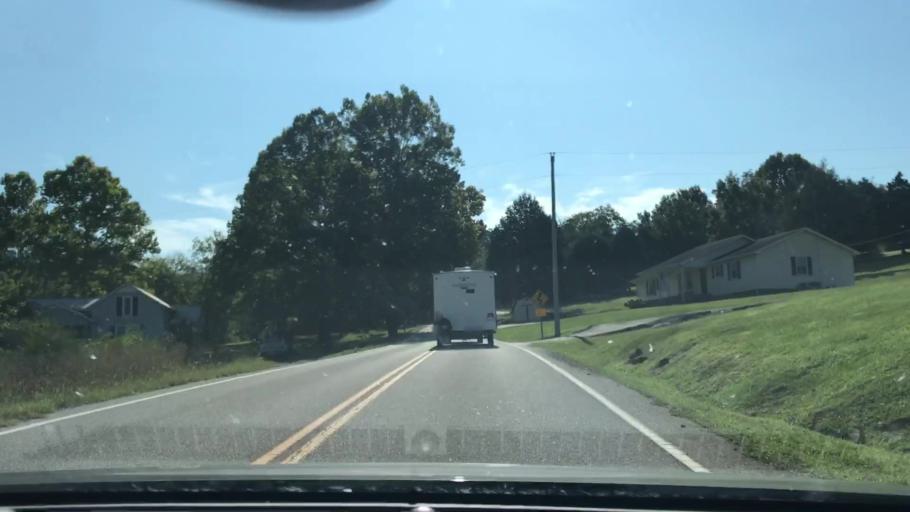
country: US
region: Tennessee
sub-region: Smith County
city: Carthage
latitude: 36.3462
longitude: -85.8608
